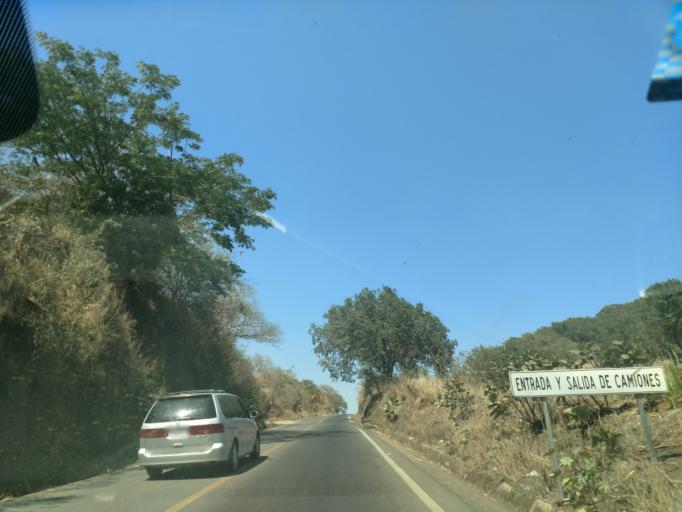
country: MX
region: Nayarit
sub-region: Tepic
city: La Corregidora
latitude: 21.5003
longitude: -104.7725
